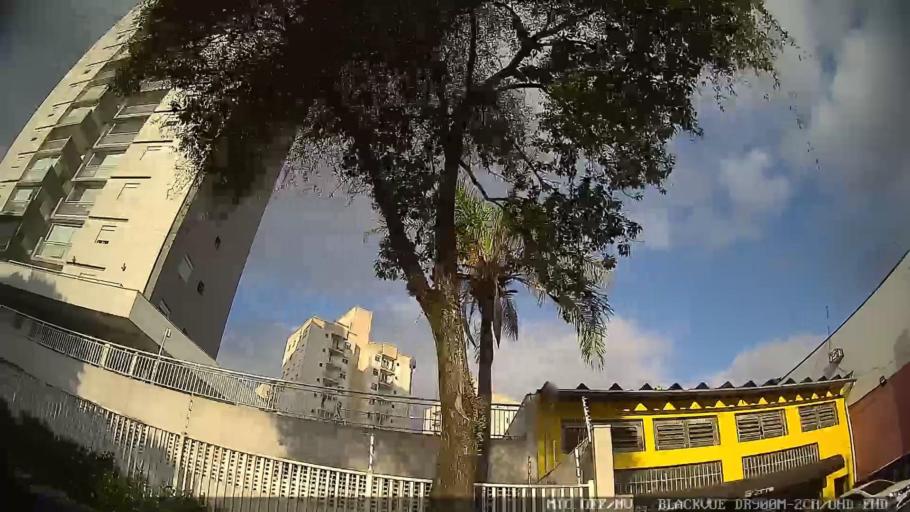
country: BR
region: Sao Paulo
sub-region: Taboao Da Serra
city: Taboao da Serra
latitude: -23.6178
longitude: -46.7570
